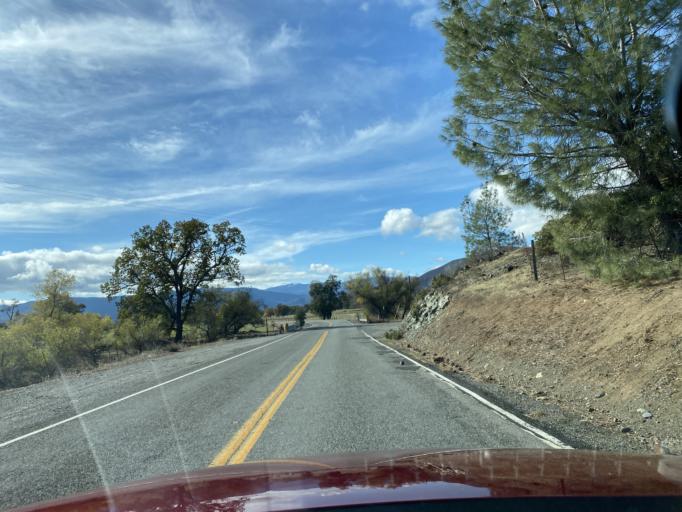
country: US
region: California
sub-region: Glenn County
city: Willows
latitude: 39.4073
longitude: -122.5486
